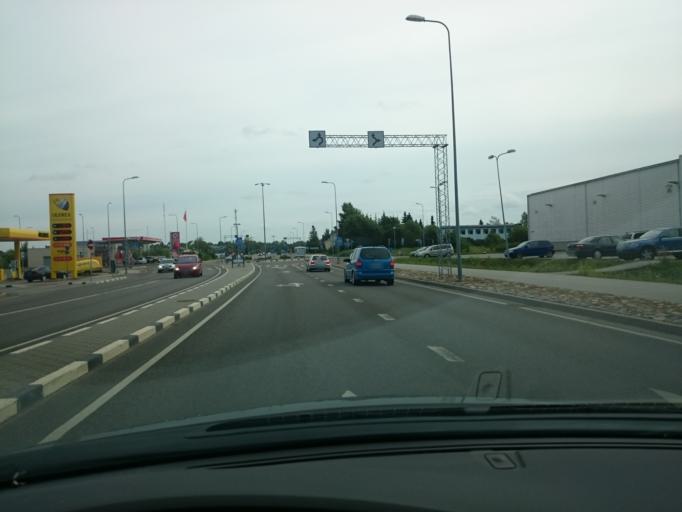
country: EE
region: Laeaene
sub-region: Ridala Parish
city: Uuemoisa
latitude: 58.9378
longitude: 23.5727
